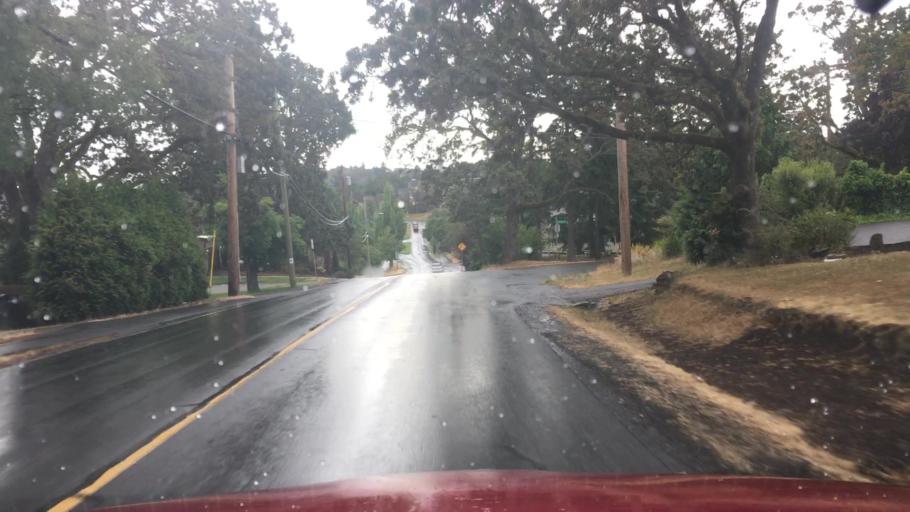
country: CA
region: British Columbia
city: Victoria
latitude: 48.4535
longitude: -123.3505
